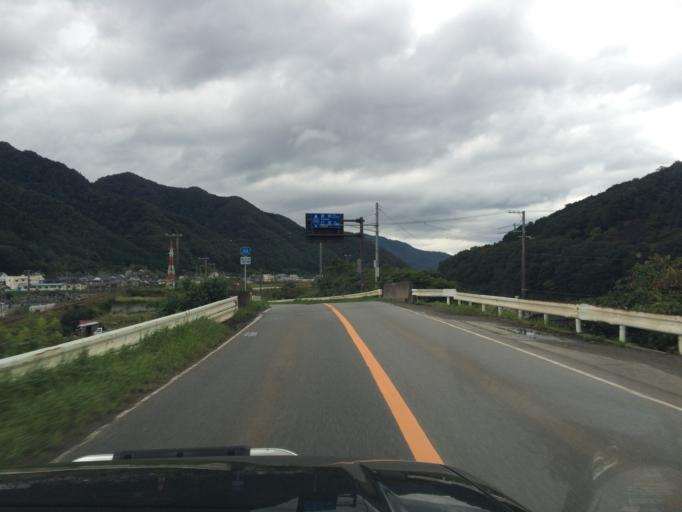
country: JP
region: Hyogo
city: Toyooka
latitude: 35.4058
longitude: 134.7776
